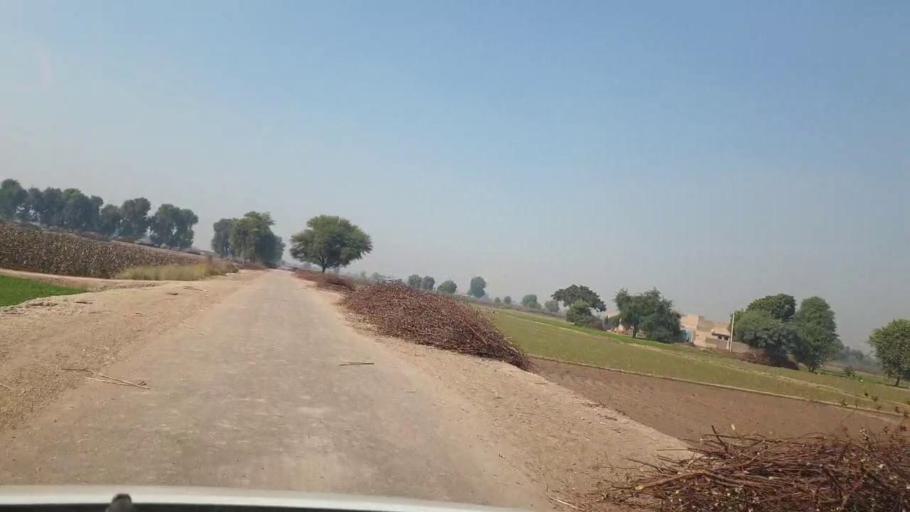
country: PK
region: Sindh
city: Bhan
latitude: 26.6116
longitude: 67.7662
